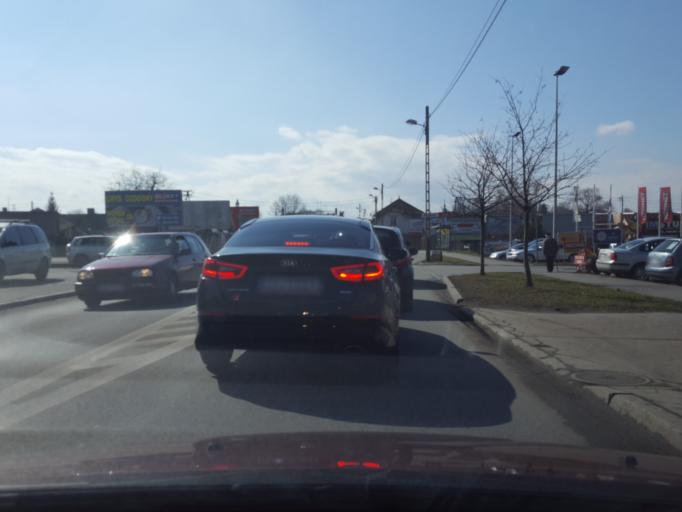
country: PL
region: Lesser Poland Voivodeship
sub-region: Powiat nowosadecki
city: Nowy Sacz
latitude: 49.6325
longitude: 20.6919
